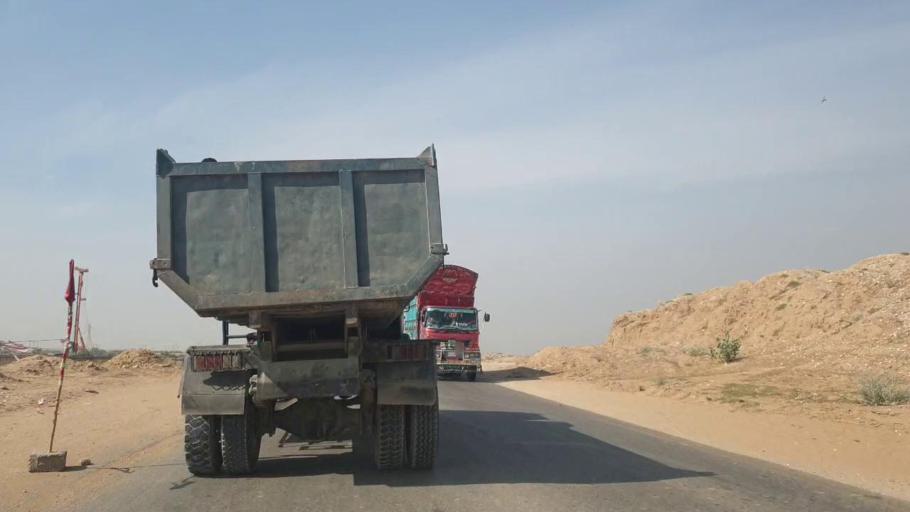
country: PK
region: Sindh
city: Sann
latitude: 26.0321
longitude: 68.1210
